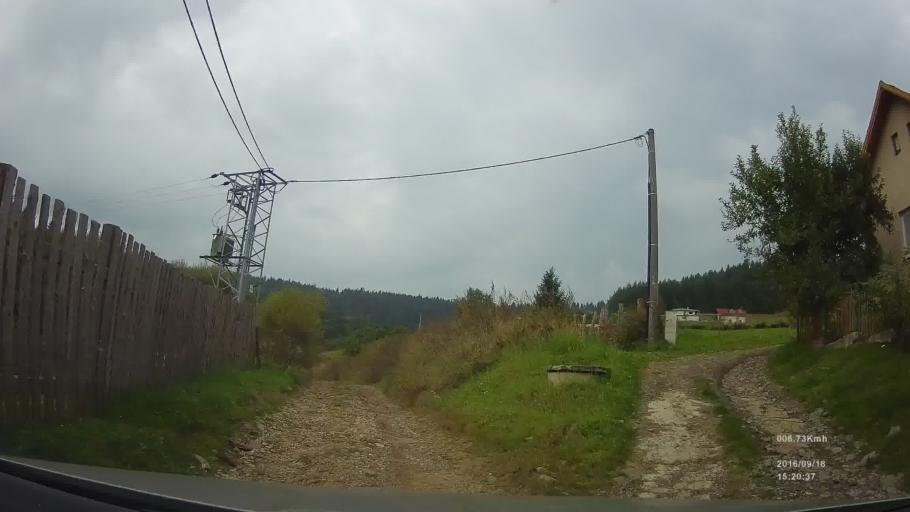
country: SK
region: Presovsky
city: Lubica
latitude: 49.0411
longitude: 20.4871
